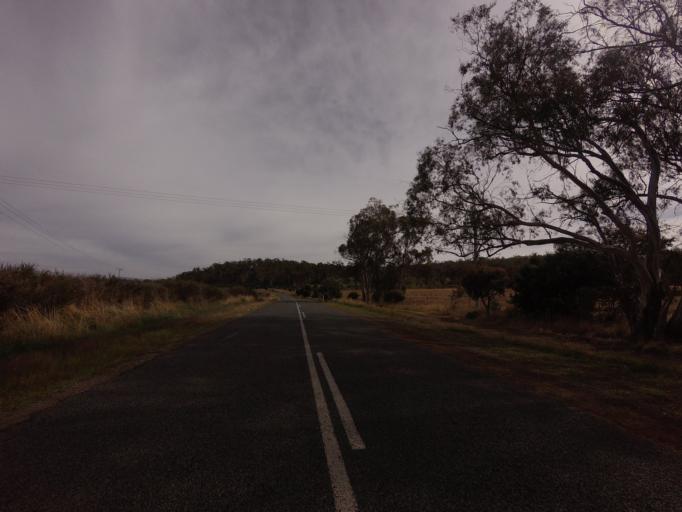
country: AU
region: Tasmania
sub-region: Brighton
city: Bridgewater
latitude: -42.3360
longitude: 147.4017
